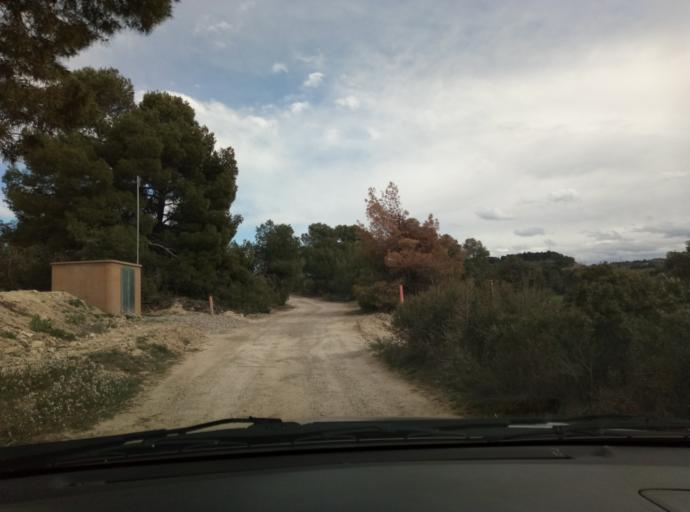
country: ES
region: Catalonia
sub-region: Provincia de Lleida
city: Ciutadilla
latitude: 41.5782
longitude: 1.1200
